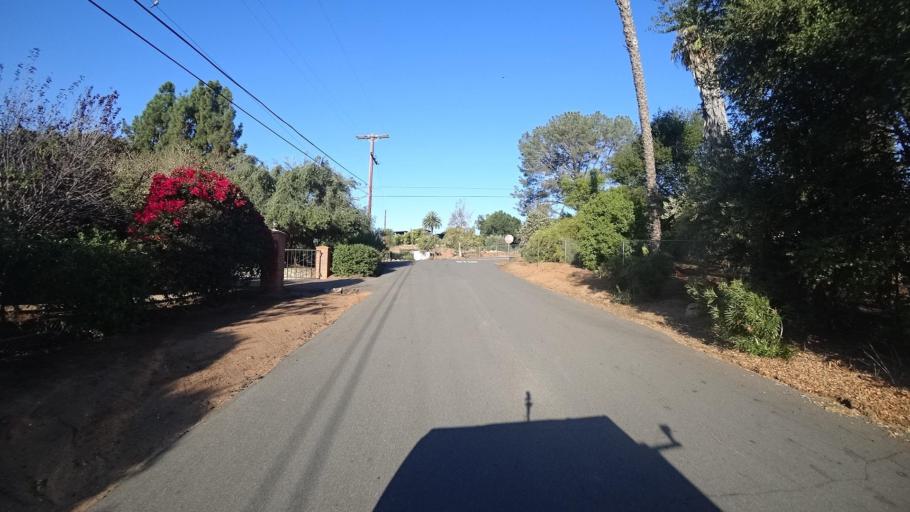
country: US
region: California
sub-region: San Diego County
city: Casa de Oro-Mount Helix
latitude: 32.7698
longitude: -116.9654
